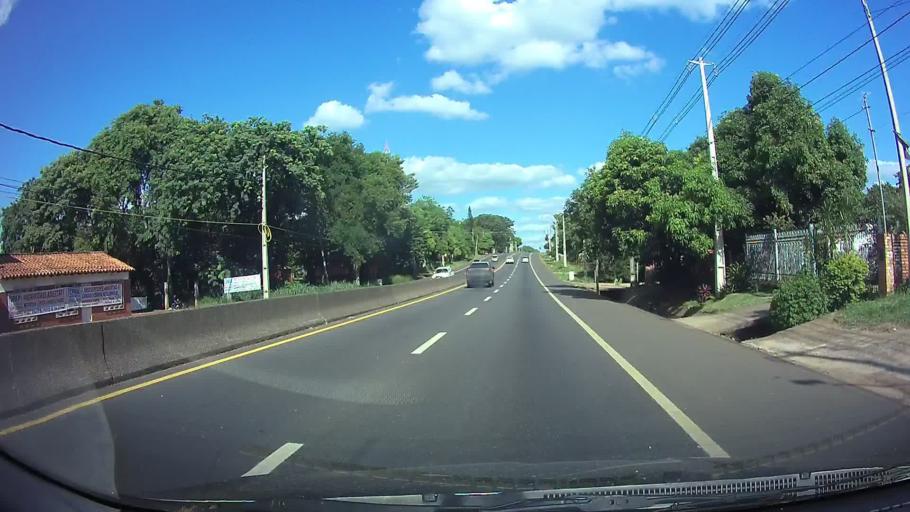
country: PY
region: Central
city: Itaugua
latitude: -25.3994
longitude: -57.3260
